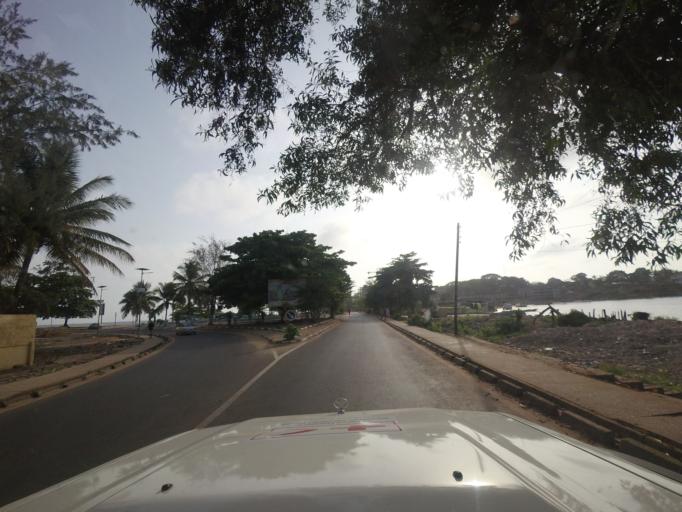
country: SL
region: Western Area
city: Freetown
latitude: 8.4936
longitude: -13.2921
